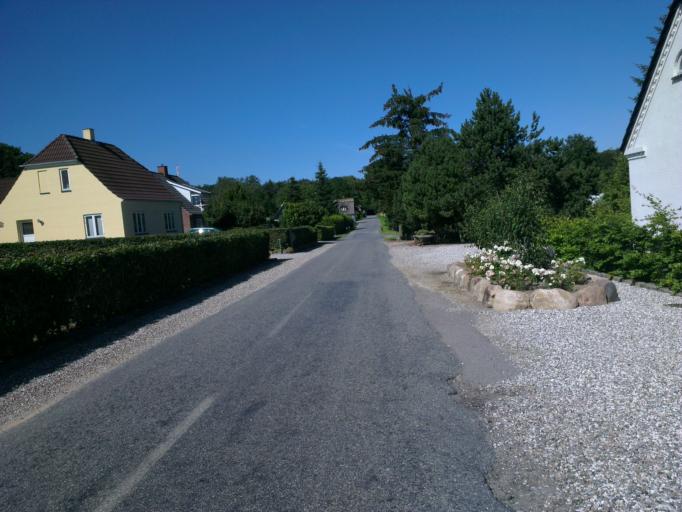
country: DK
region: Capital Region
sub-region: Frederikssund Kommune
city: Skibby
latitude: 55.7141
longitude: 11.9498
